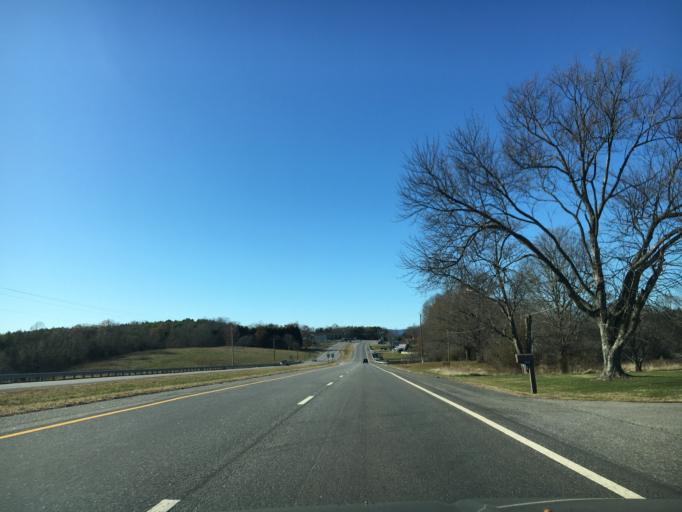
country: US
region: Virginia
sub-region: Patrick County
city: Patrick Springs
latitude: 36.6113
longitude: -80.1794
